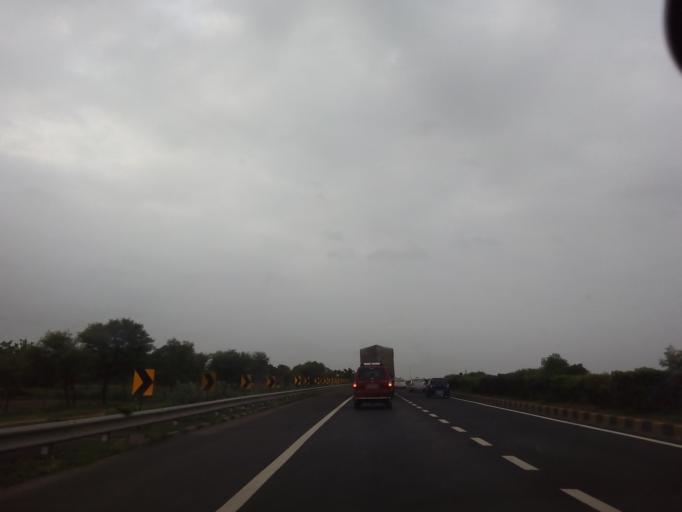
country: IN
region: Gujarat
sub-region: Kheda
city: Mahemdavad
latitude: 22.8208
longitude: 72.8305
